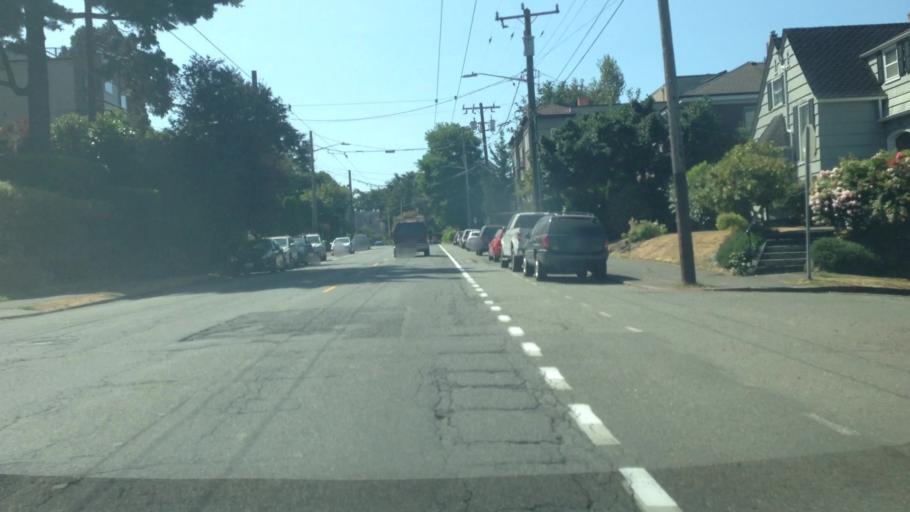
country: US
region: Washington
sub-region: King County
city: Seattle
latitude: 47.6351
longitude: -122.3201
